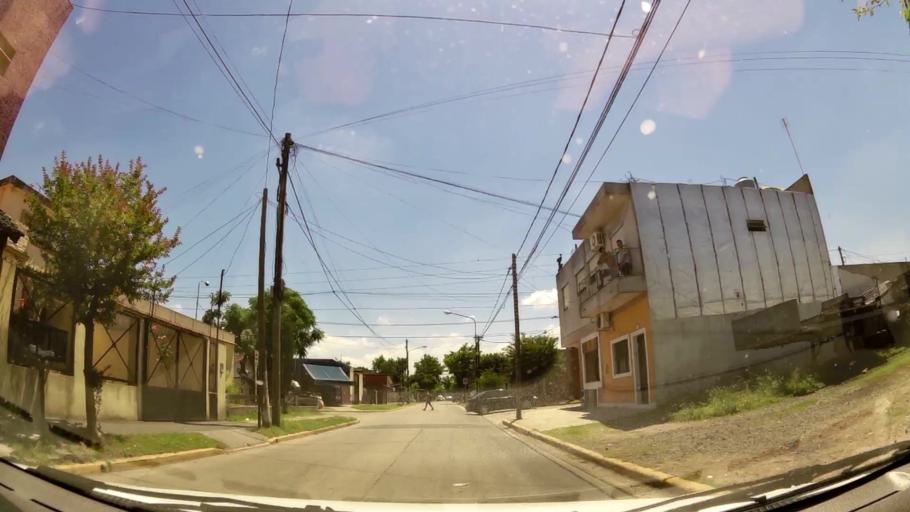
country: AR
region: Buenos Aires
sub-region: Partido de Merlo
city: Merlo
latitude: -34.6612
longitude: -58.7135
